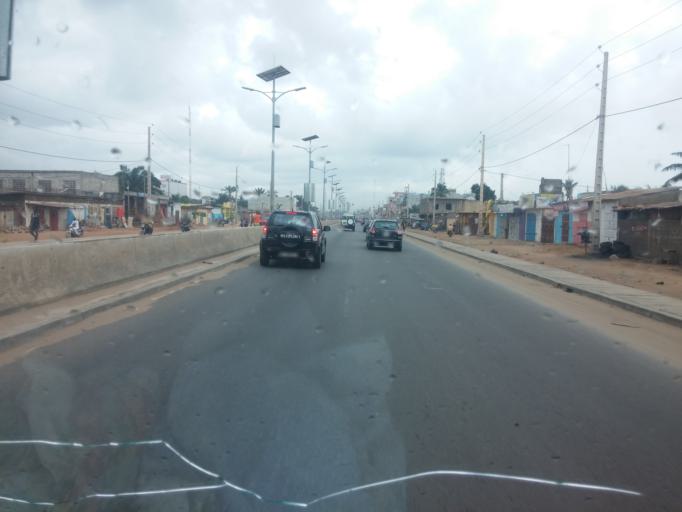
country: BJ
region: Atlantique
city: Hevie
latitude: 6.3888
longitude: 2.3153
